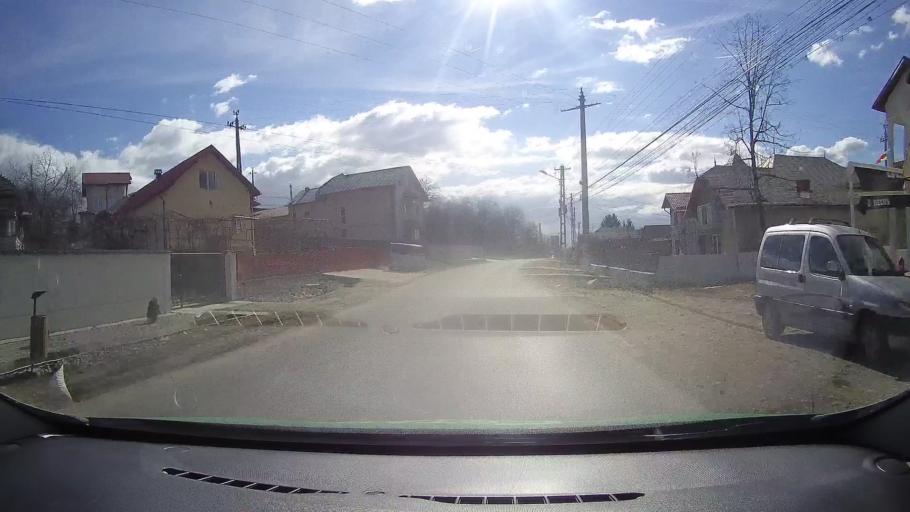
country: RO
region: Dambovita
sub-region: Comuna Vulcana-Pandele
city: Gura Vulcanei
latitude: 45.0275
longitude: 25.3953
